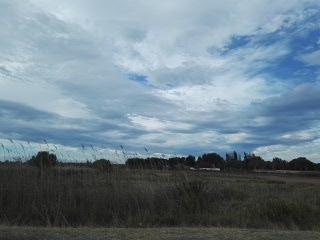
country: FR
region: Languedoc-Roussillon
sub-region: Departement de l'Herault
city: Marseillan
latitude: 43.3143
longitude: 3.5376
